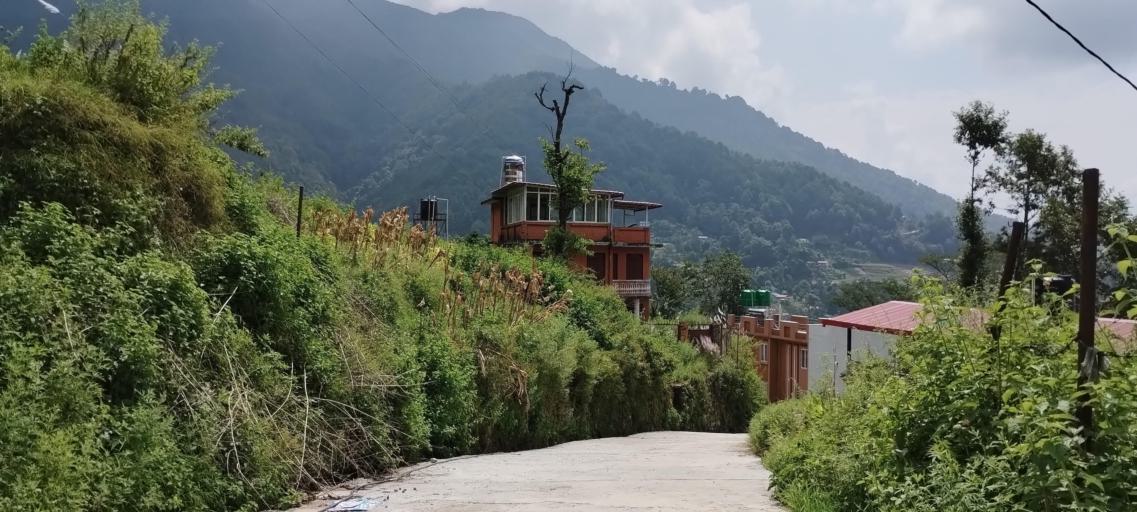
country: NP
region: Central Region
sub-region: Bagmati Zone
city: Kathmandu
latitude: 27.7904
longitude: 85.3647
